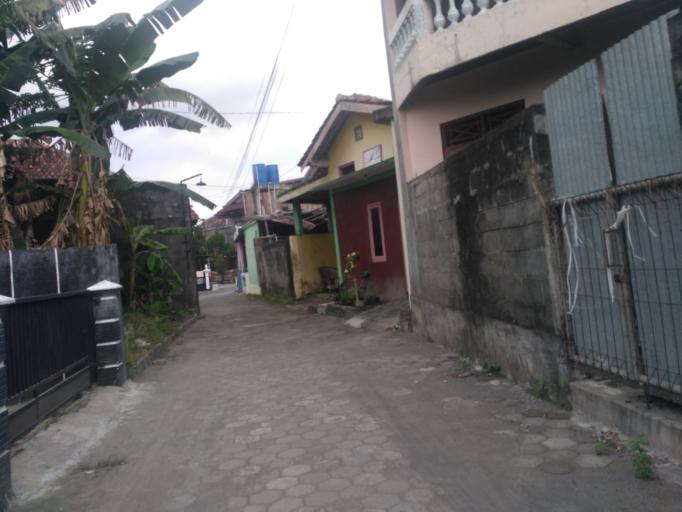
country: ID
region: Daerah Istimewa Yogyakarta
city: Melati
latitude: -7.7546
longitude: 110.3649
